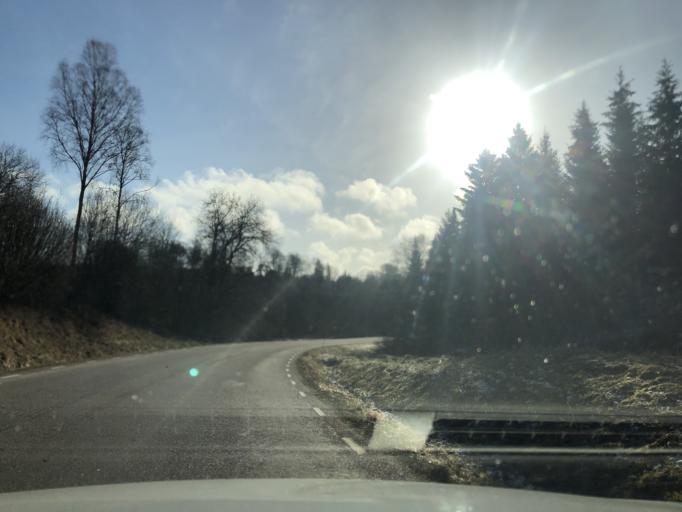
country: SE
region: Vaestra Goetaland
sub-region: Ulricehamns Kommun
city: Ulricehamn
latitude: 57.8090
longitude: 13.5431
